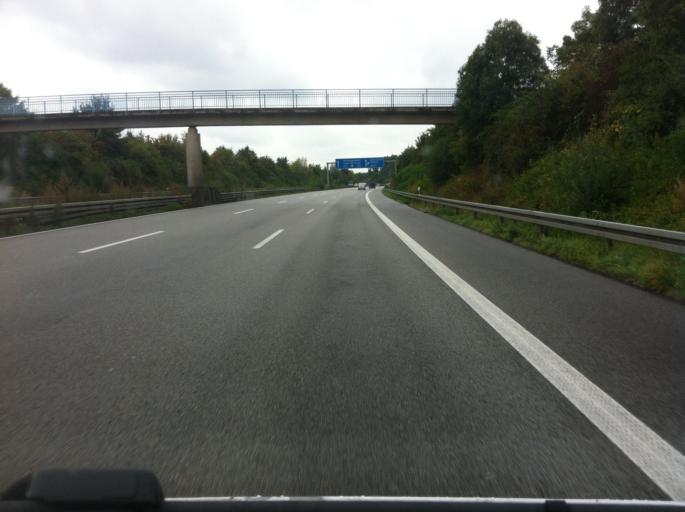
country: DE
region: North Rhine-Westphalia
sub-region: Regierungsbezirk Dusseldorf
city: Meerbusch
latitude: 51.2891
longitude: 6.6695
